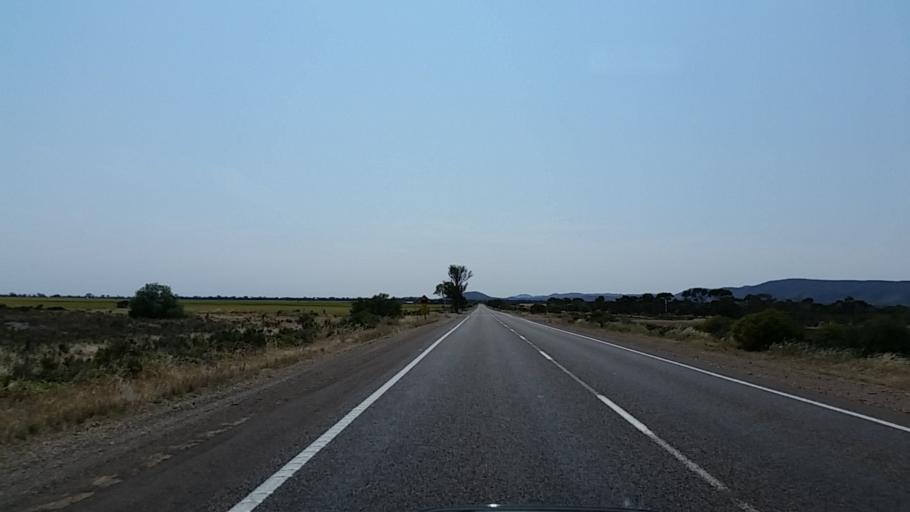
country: AU
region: South Australia
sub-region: Port Pirie City and Dists
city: Port Pirie
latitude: -32.8903
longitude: 137.9823
